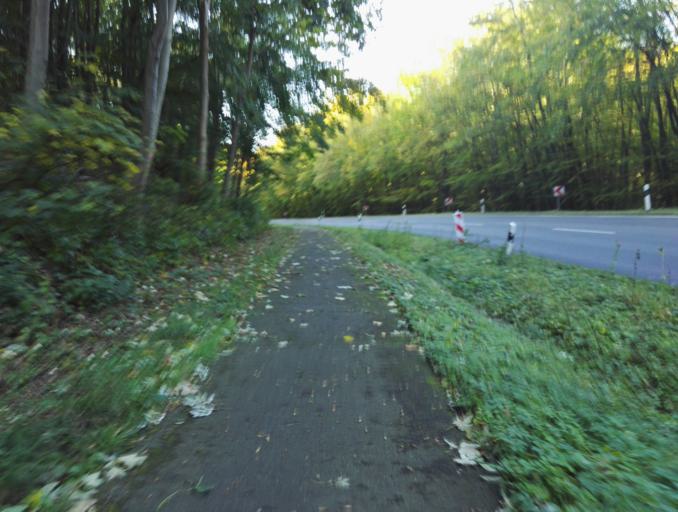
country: DE
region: Lower Saxony
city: Schellerten
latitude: 52.1281
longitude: 10.0909
